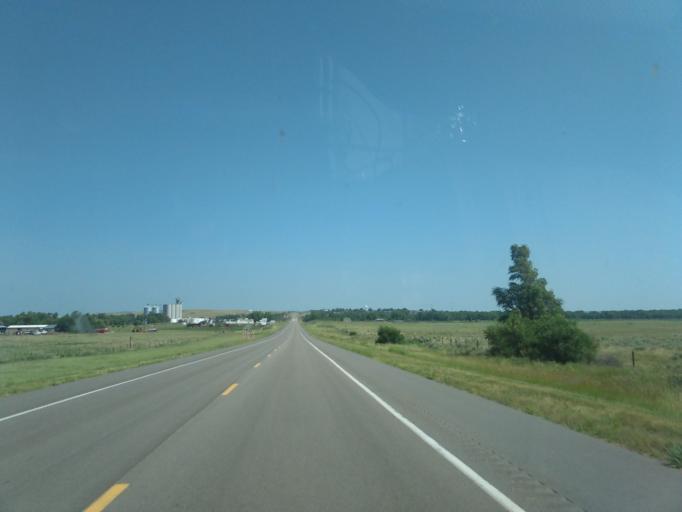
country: US
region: Nebraska
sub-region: Dundy County
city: Benkelman
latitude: 40.0262
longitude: -101.5429
